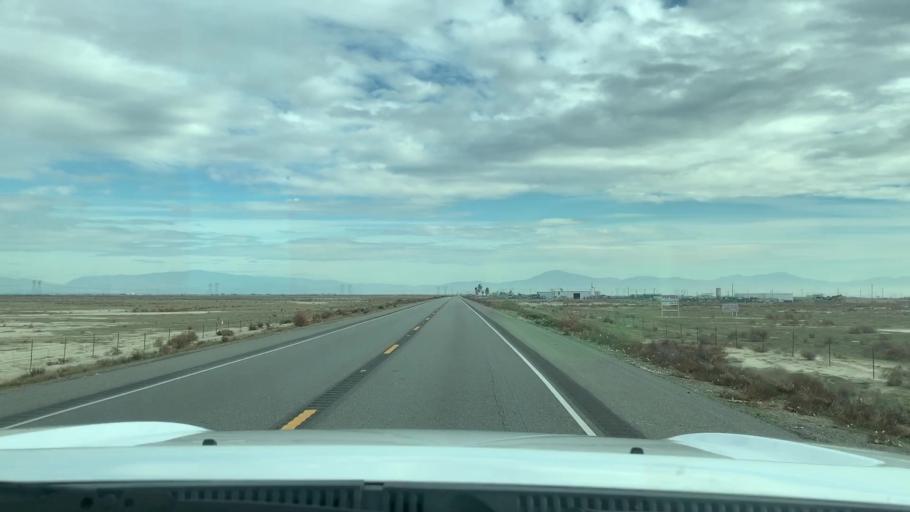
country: US
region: California
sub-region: Kern County
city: Rosedale
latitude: 35.2674
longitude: -119.2703
